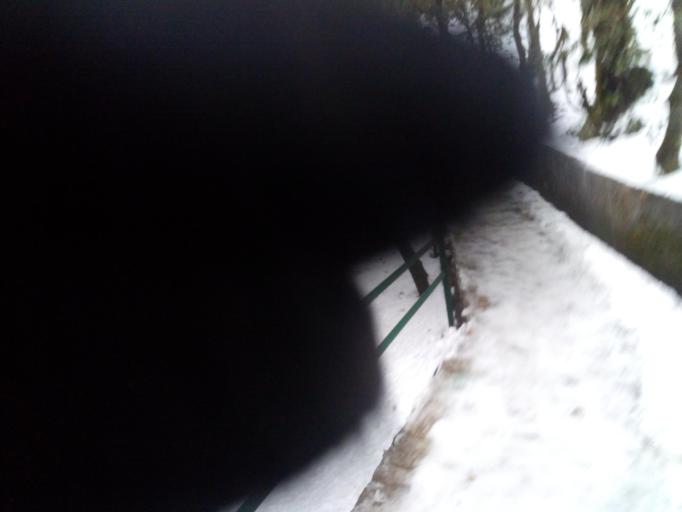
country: IN
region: Himachal Pradesh
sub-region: Shimla
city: Theog
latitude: 31.0959
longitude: 77.2644
